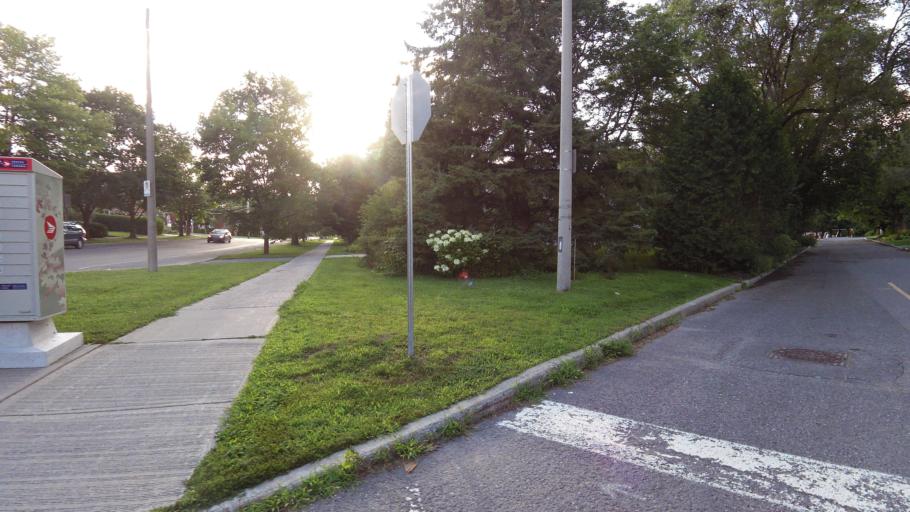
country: CA
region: Ontario
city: Ottawa
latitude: 45.3967
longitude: -75.7176
